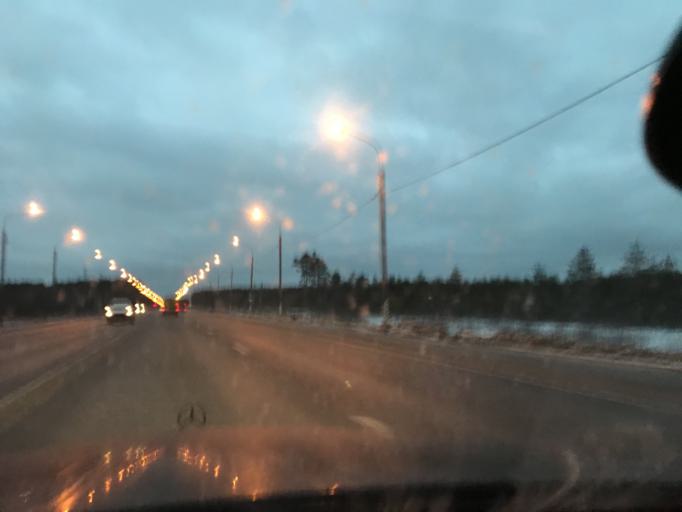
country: RU
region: Vladimir
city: Pokrov
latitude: 55.9235
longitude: 39.2546
